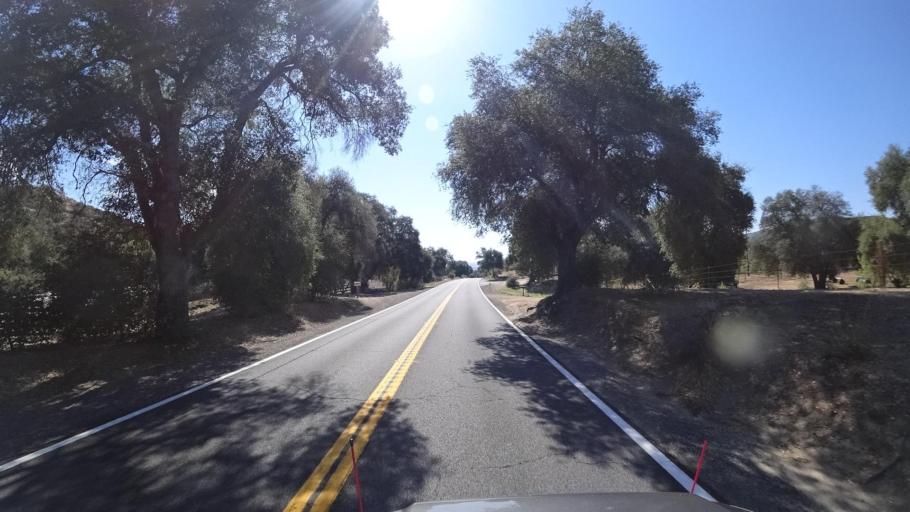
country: US
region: California
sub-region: Riverside County
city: Aguanga
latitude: 33.3456
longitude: -116.7290
